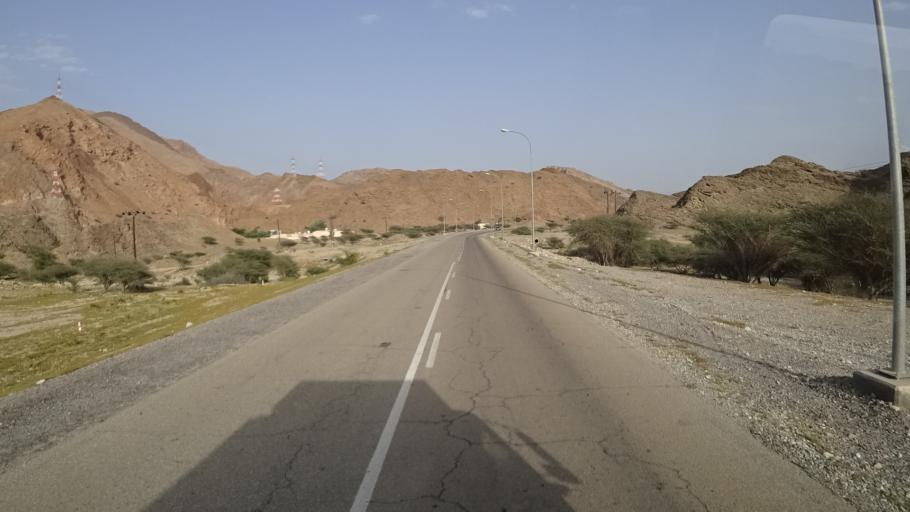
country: OM
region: Muhafazat Masqat
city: Bawshar
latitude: 23.3705
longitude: 58.5219
